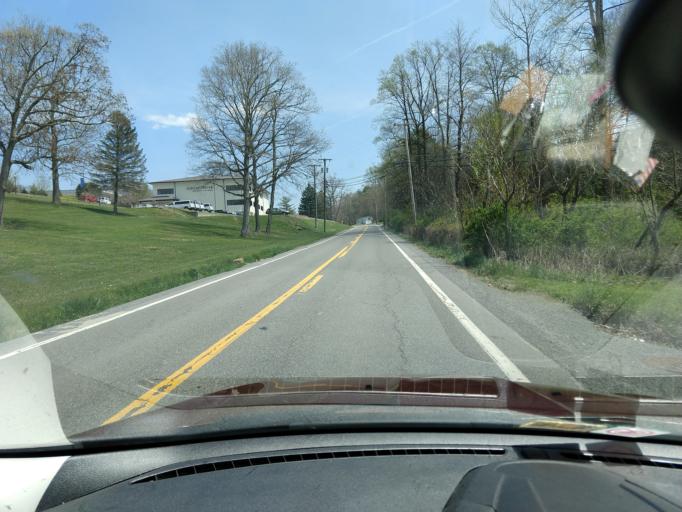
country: US
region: West Virginia
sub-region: Raleigh County
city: Bradley
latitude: 37.8526
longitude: -81.2023
